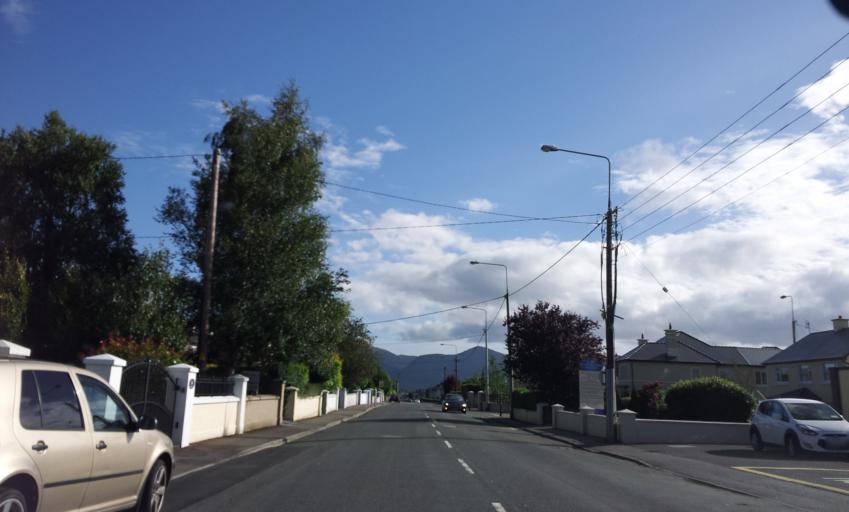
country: IE
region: Munster
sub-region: Ciarrai
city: Cill Airne
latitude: 52.0661
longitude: -9.5060
